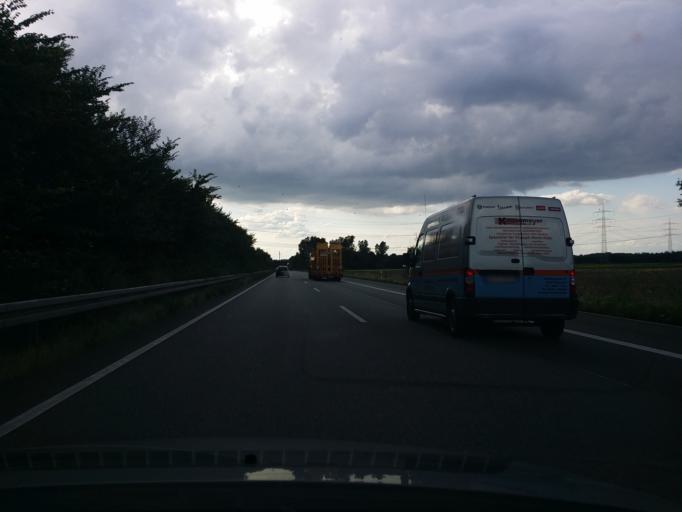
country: DE
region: Hesse
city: Griesheim
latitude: 49.8873
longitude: 8.5548
